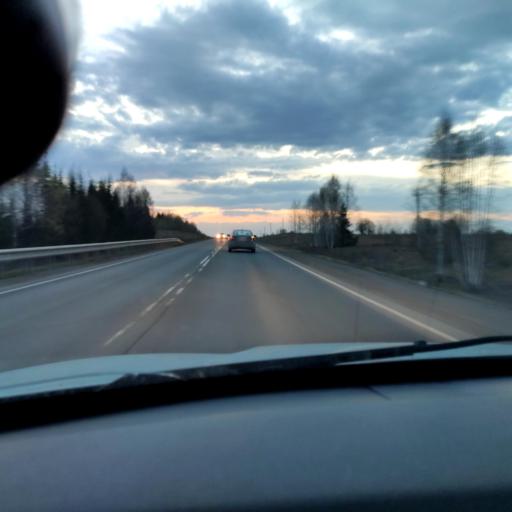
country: RU
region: Perm
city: Verkhnechusovskiye Gorodki
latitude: 58.2384
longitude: 57.0744
